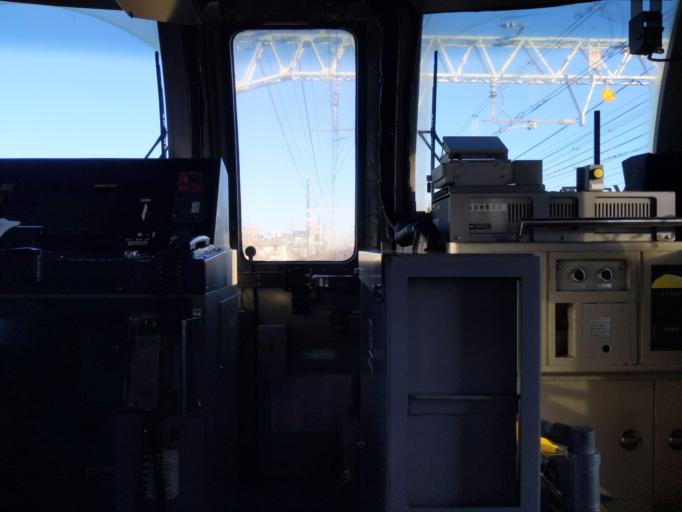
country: JP
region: Chiba
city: Funabashi
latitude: 35.7117
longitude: 139.9496
